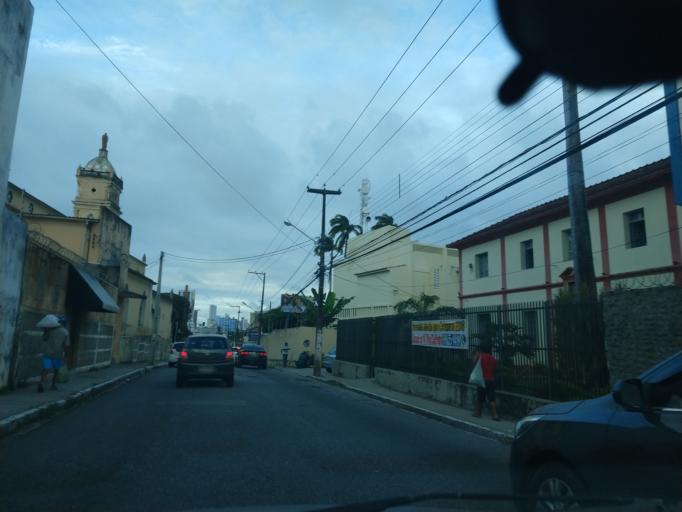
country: BR
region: Rio Grande do Norte
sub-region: Natal
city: Natal
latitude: -5.7934
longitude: -35.2131
